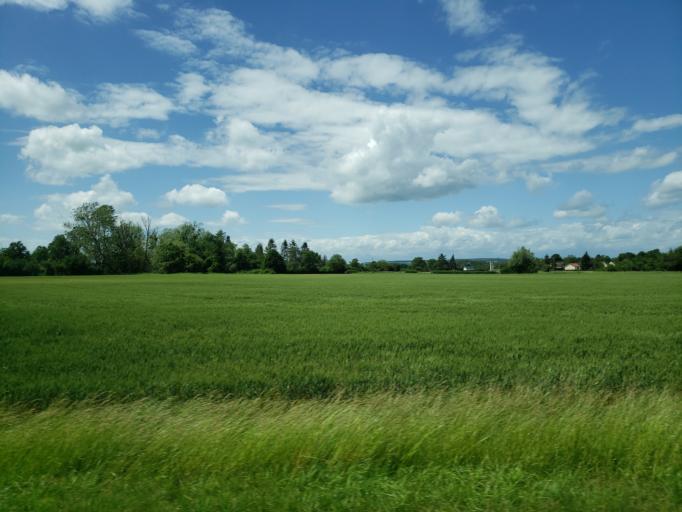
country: FR
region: Bourgogne
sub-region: Departement de l'Yonne
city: Migennes
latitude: 47.9494
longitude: 3.5029
